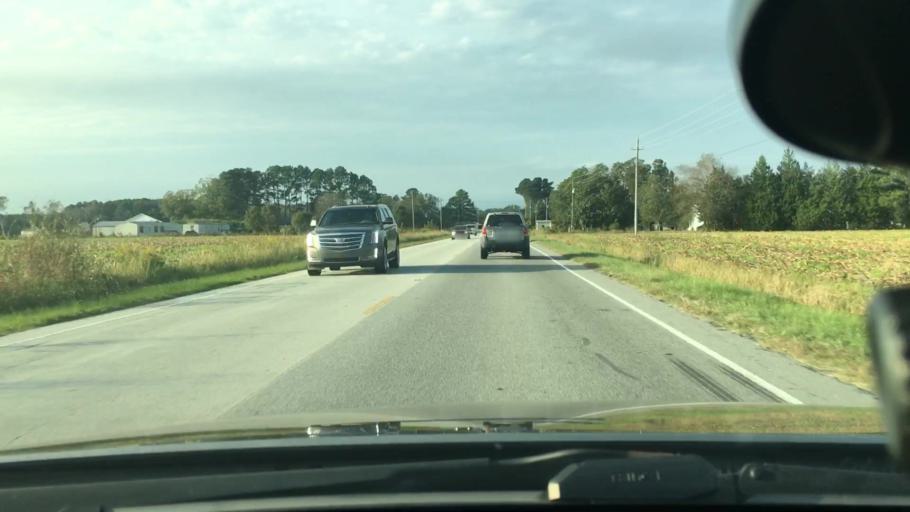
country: US
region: North Carolina
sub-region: Pitt County
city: Windsor
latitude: 35.5031
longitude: -77.3136
